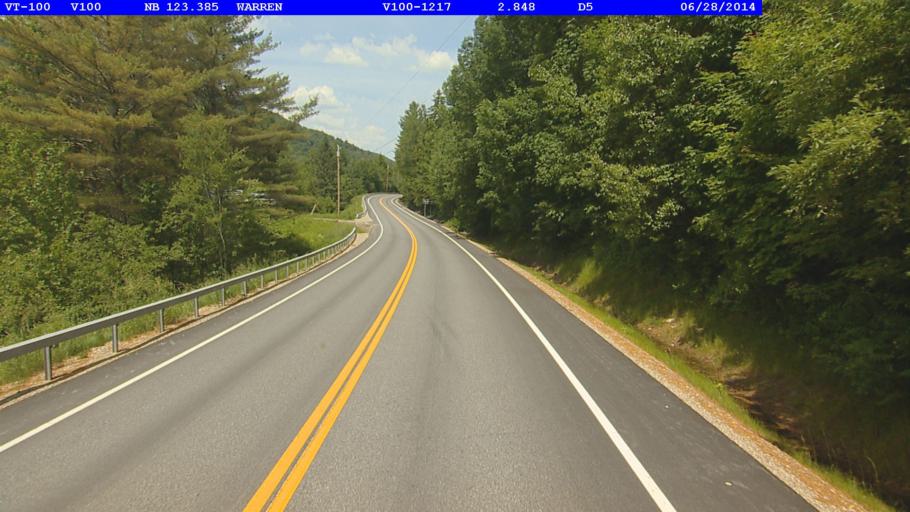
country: US
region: Vermont
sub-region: Washington County
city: Northfield
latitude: 44.0996
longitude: -72.8609
